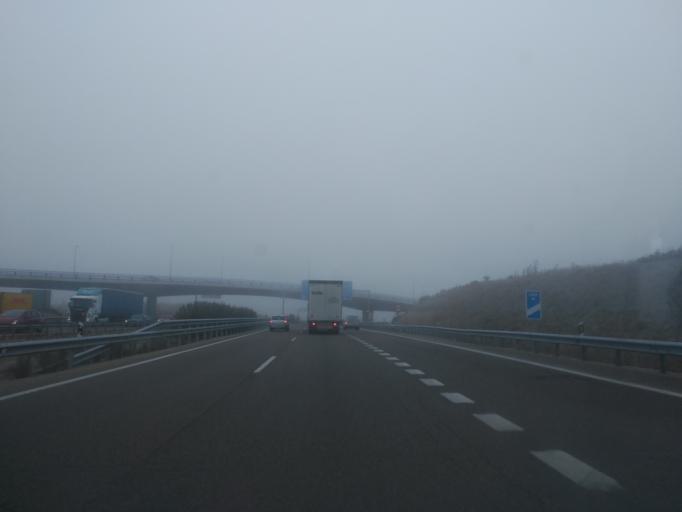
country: ES
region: Castille and Leon
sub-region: Provincia de Valladolid
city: Arroyo
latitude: 41.6190
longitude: -4.7898
